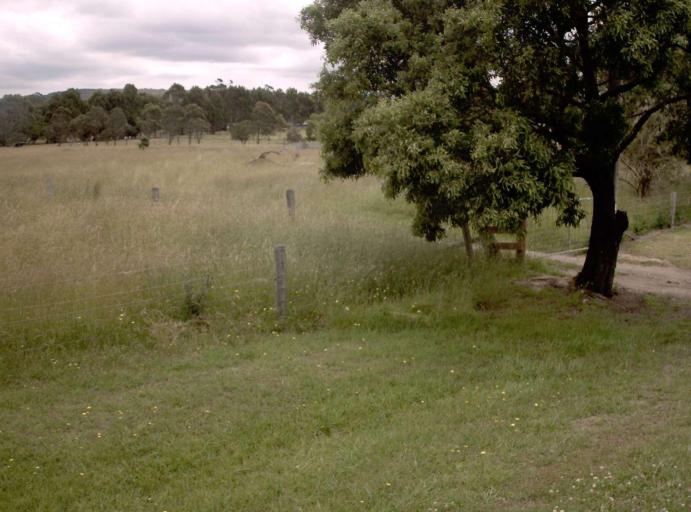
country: AU
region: Victoria
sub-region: Latrobe
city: Traralgon
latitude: -38.5234
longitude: 146.6602
